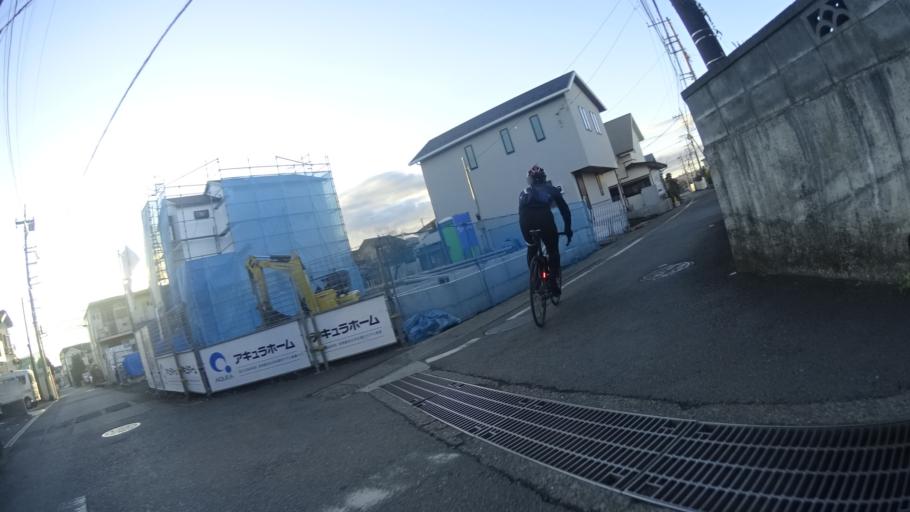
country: JP
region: Kanagawa
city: Atsugi
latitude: 35.4645
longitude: 139.3692
